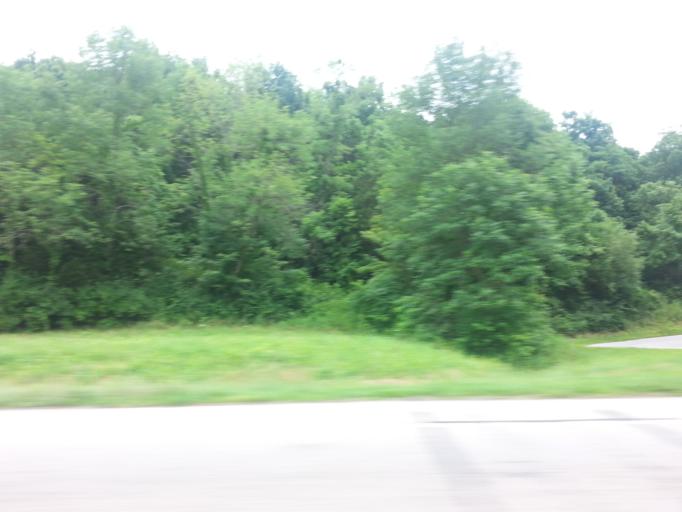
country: US
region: Ohio
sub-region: Brown County
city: Aberdeen
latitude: 38.6996
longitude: -83.7843
